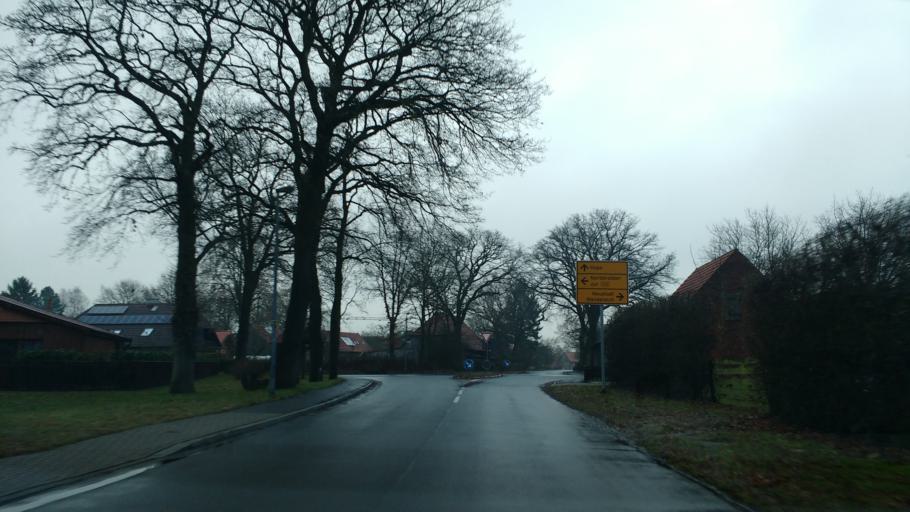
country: DE
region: Lower Saxony
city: Schwarmstedt
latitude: 52.6430
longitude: 9.5726
